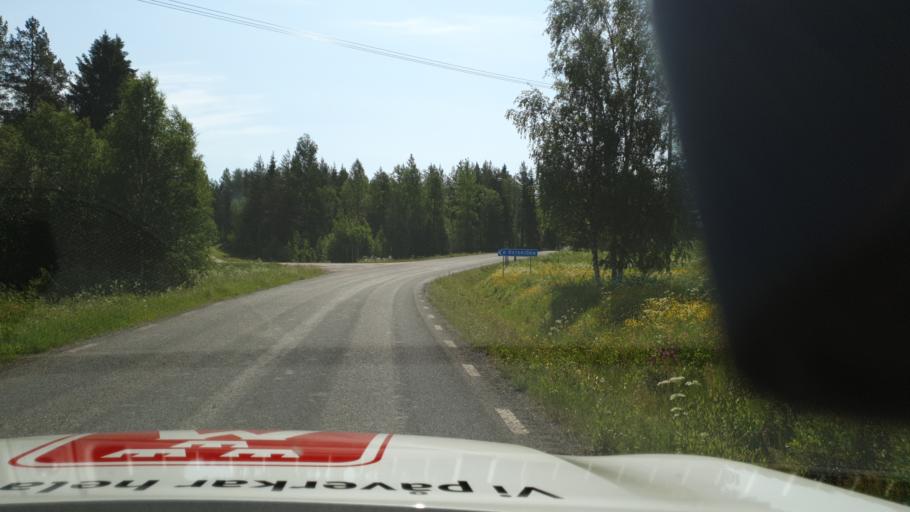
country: SE
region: Vaesterbotten
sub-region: Skelleftea Kommun
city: Langsele
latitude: 65.0056
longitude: 20.0896
